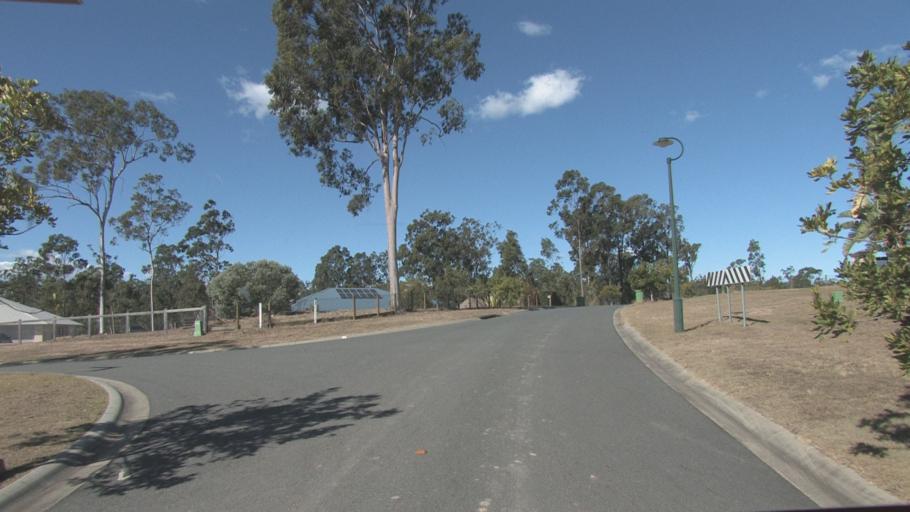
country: AU
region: Queensland
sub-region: Logan
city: North Maclean
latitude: -27.7529
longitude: 152.9337
